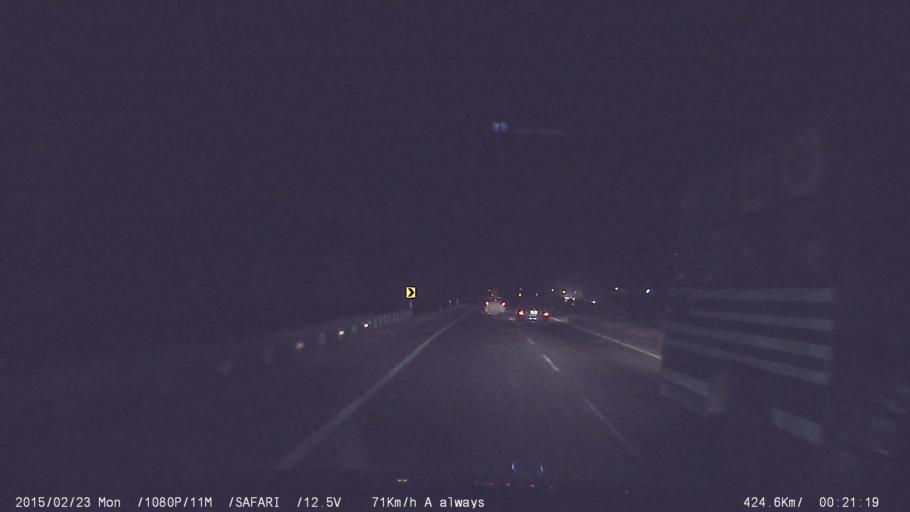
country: IN
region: Tamil Nadu
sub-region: Salem
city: Omalur
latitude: 11.8988
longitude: 78.0629
